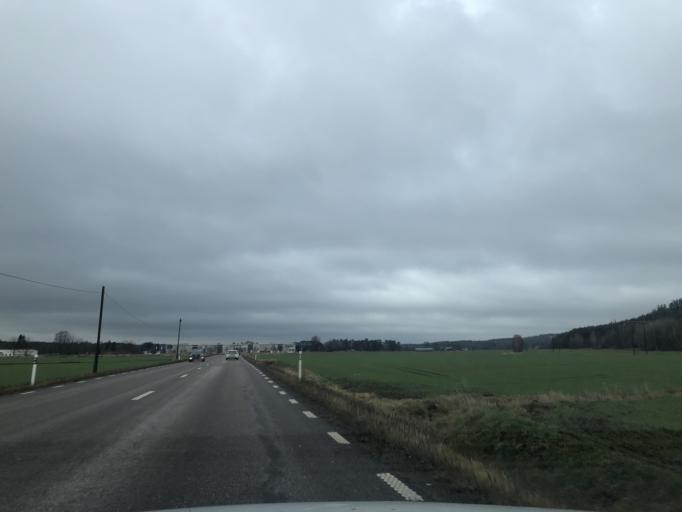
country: SE
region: Vaestra Goetaland
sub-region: Ulricehamns Kommun
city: Ulricehamn
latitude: 57.8397
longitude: 13.4373
